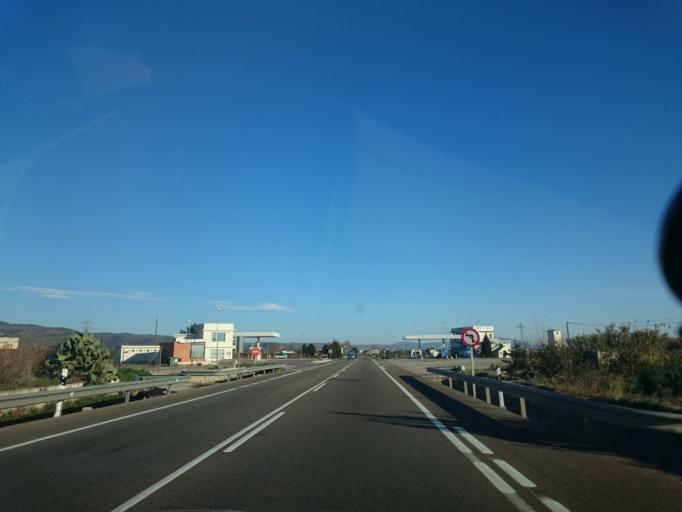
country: ES
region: Valencia
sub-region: Provincia de Castello
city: Orpesa/Oropesa del Mar
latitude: 40.1340
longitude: 0.1490
